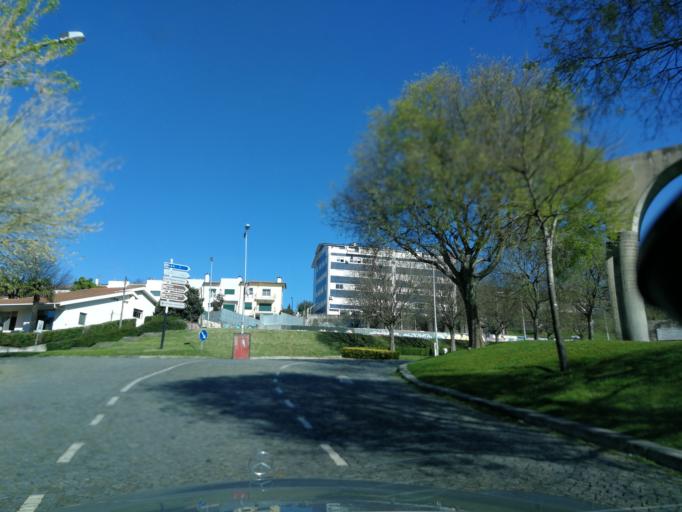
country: PT
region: Braga
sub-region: Braga
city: Braga
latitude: 41.5445
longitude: -8.4284
